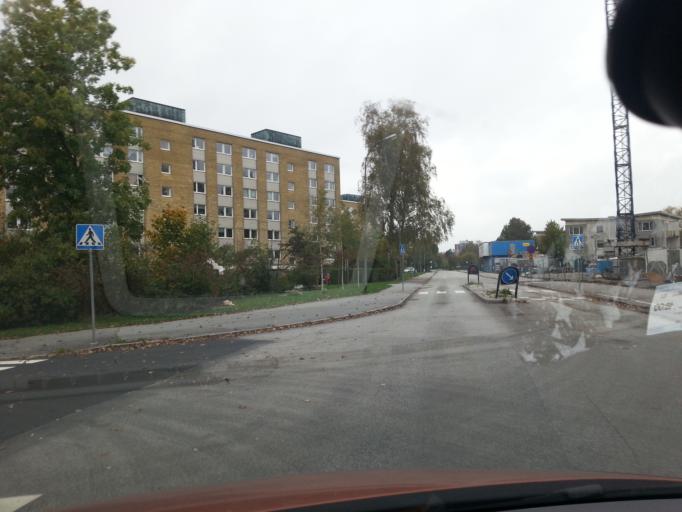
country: SE
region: Skane
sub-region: Lunds Kommun
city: Lund
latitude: 55.6943
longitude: 13.2060
